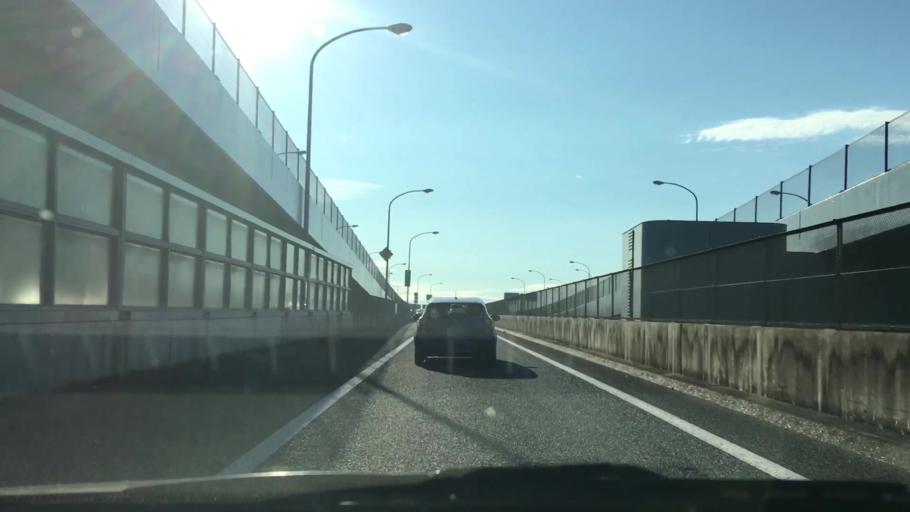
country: JP
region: Tokyo
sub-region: Machida-shi
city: Machida
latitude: 35.5489
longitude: 139.5361
